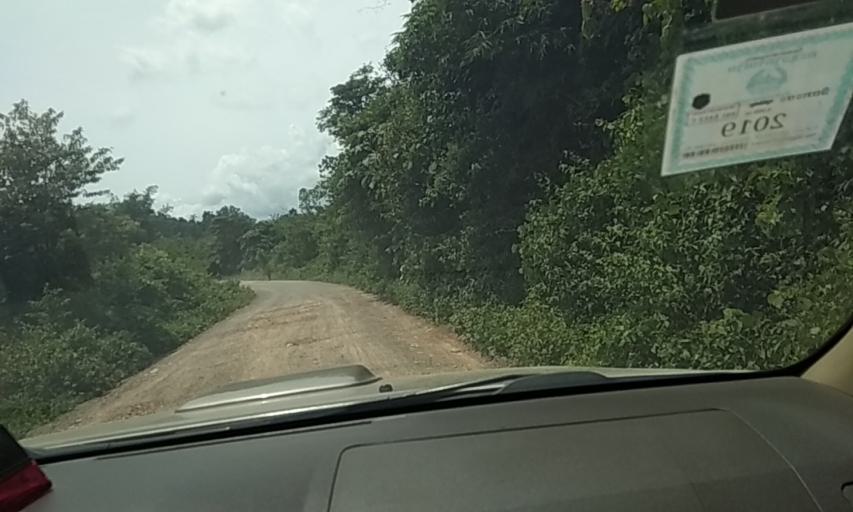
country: LA
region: Bolikhamxai
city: Ban Nahin
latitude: 18.1500
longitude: 104.7347
